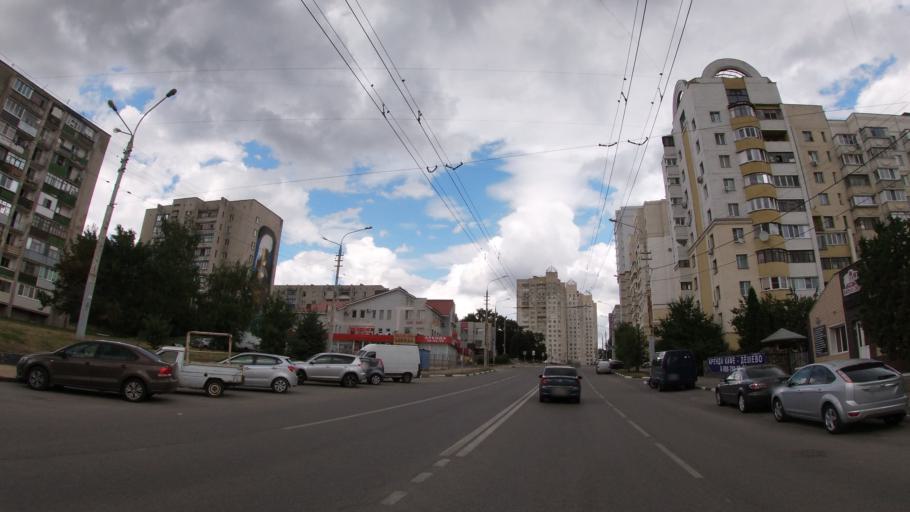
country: RU
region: Belgorod
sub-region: Belgorodskiy Rayon
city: Belgorod
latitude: 50.5981
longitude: 36.6068
